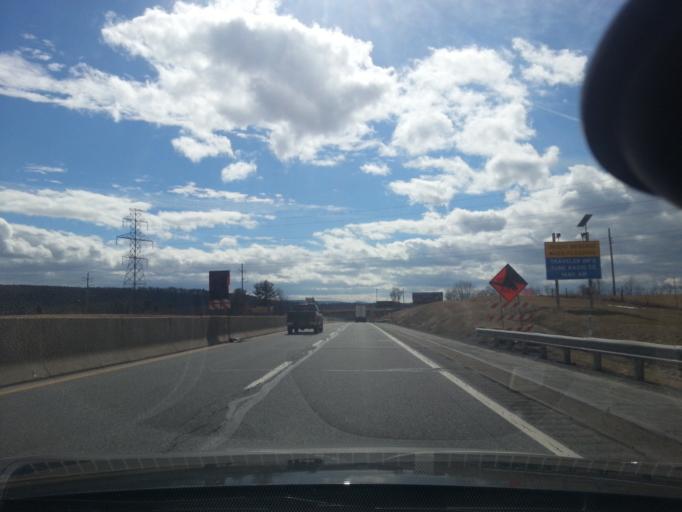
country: US
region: Pennsylvania
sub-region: Carbon County
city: Weissport East
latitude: 40.8541
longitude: -75.6533
